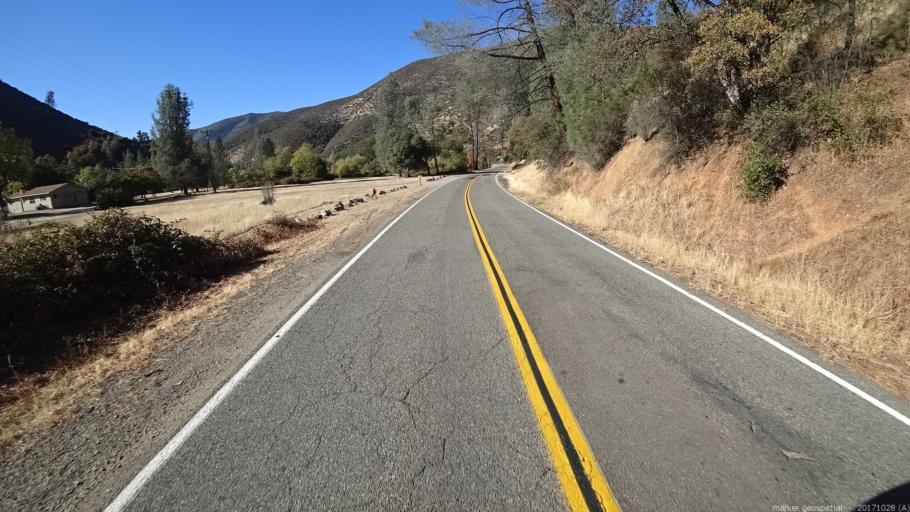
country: US
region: California
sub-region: Trinity County
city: Lewiston
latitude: 40.7180
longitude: -122.6319
